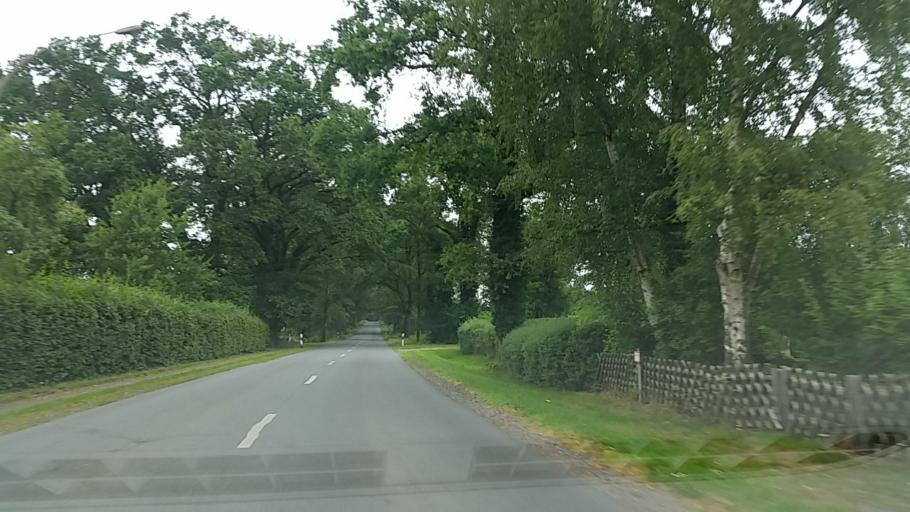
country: DE
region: Lower Saxony
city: Vollersode
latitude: 53.4138
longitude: 8.9139
